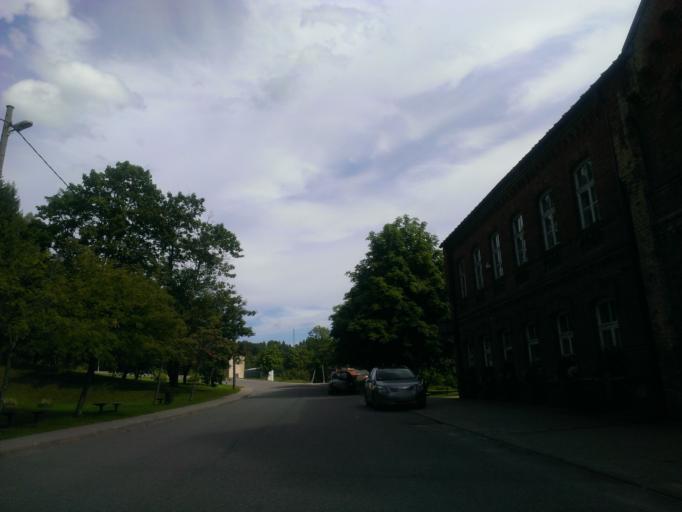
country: LV
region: Ligatne
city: Ligatne
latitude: 57.2327
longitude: 25.0431
